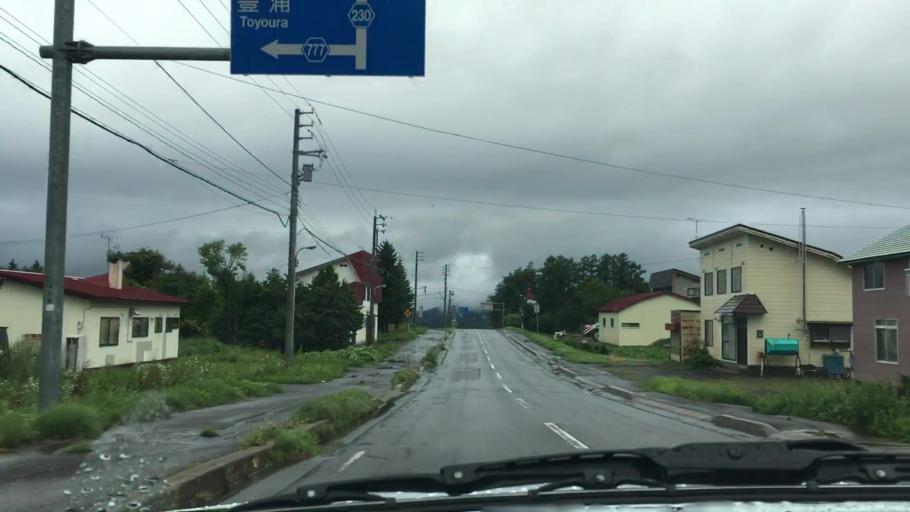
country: JP
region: Hokkaido
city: Niseko Town
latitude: 42.6946
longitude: 140.8382
